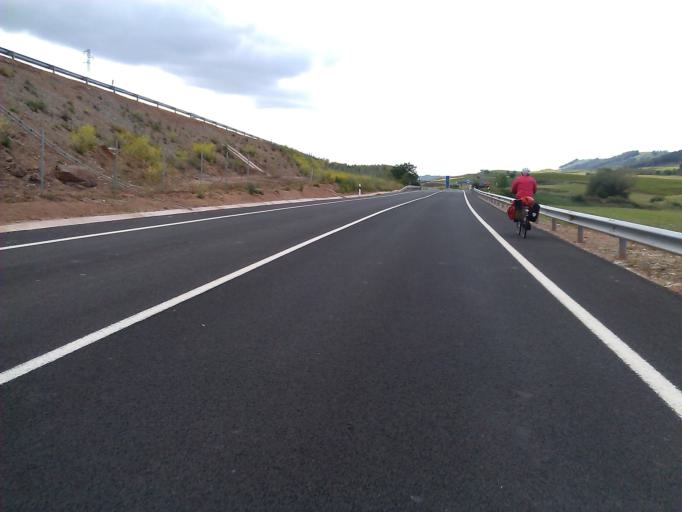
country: ES
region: La Rioja
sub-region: Provincia de La Rioja
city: Azofra
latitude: 42.4341
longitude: -2.8084
